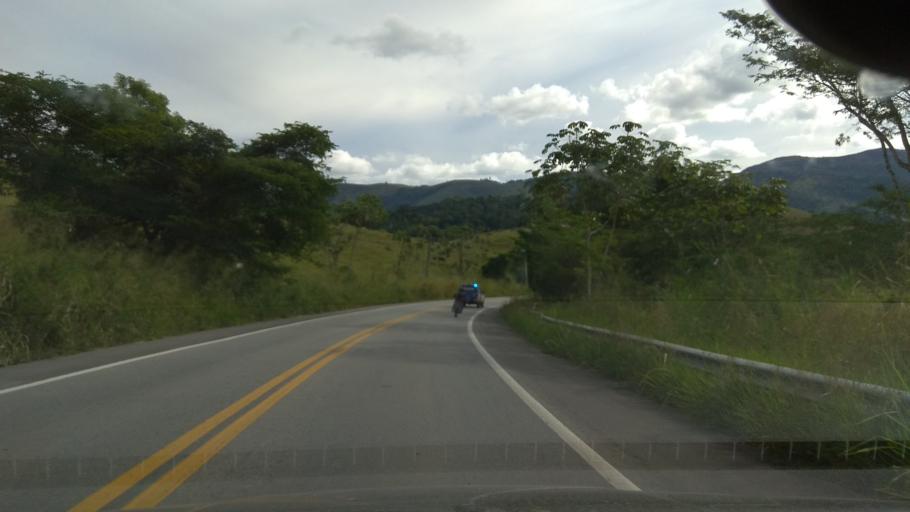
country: BR
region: Bahia
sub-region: Jitauna
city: Jitauna
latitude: -14.0080
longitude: -39.9129
